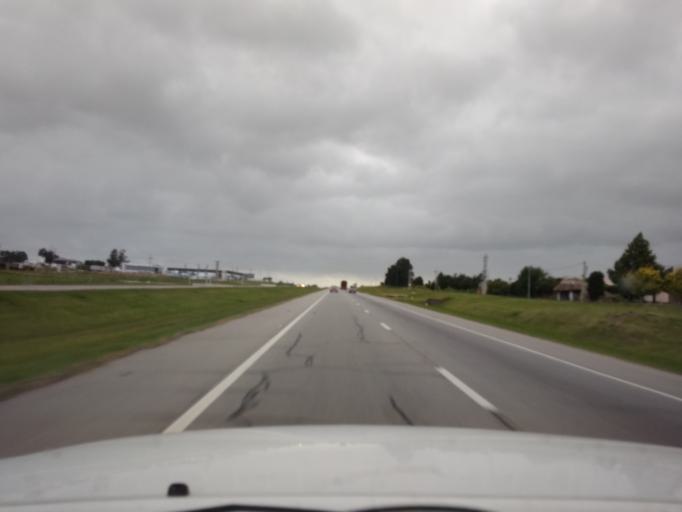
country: UY
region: Canelones
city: Las Piedras
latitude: -34.6992
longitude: -56.2394
